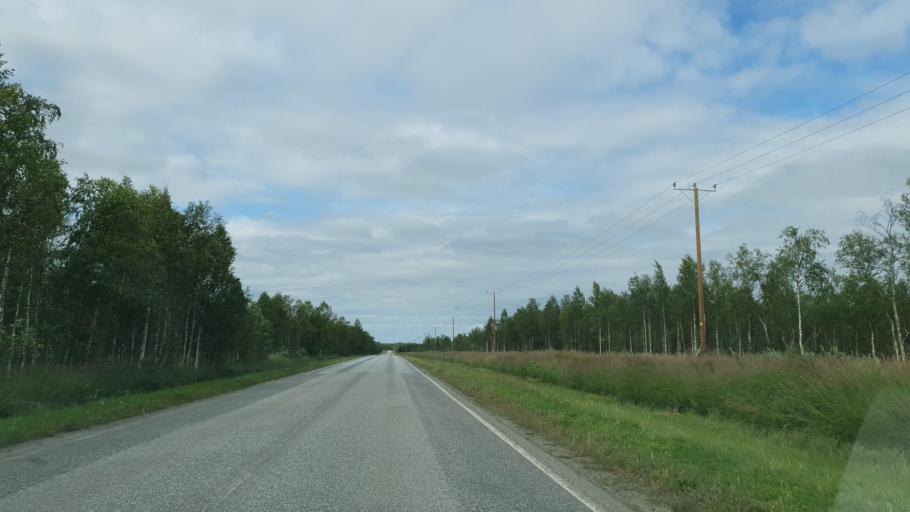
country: FI
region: Lapland
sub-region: Tunturi-Lappi
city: Kittilae
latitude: 67.6412
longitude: 25.1139
